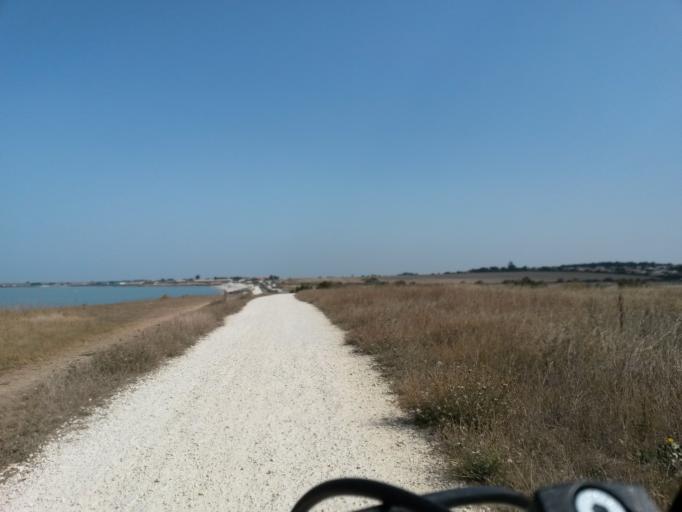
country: FR
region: Poitou-Charentes
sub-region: Departement de la Charente-Maritime
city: Nieul-sur-Mer
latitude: 46.1861
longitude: -1.2044
